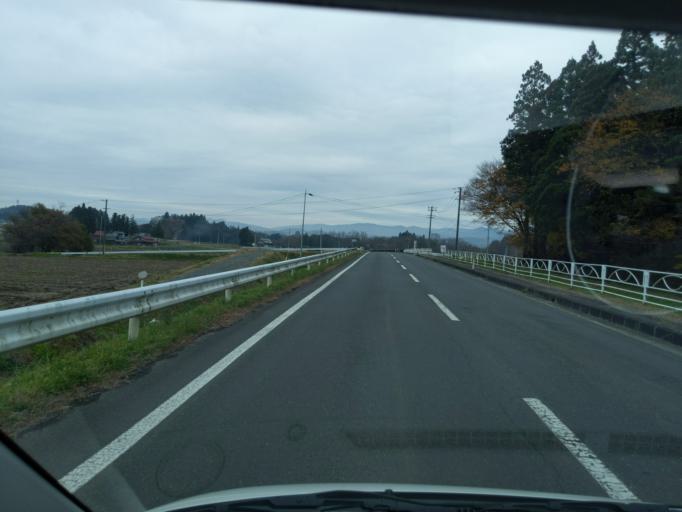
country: JP
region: Iwate
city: Mizusawa
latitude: 39.2144
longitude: 141.2235
